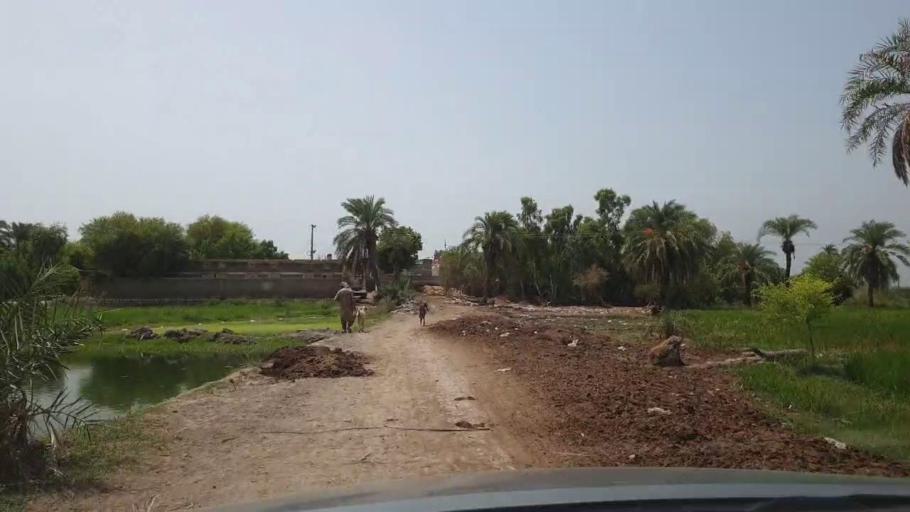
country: PK
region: Sindh
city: Madeji
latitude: 27.7874
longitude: 68.4339
